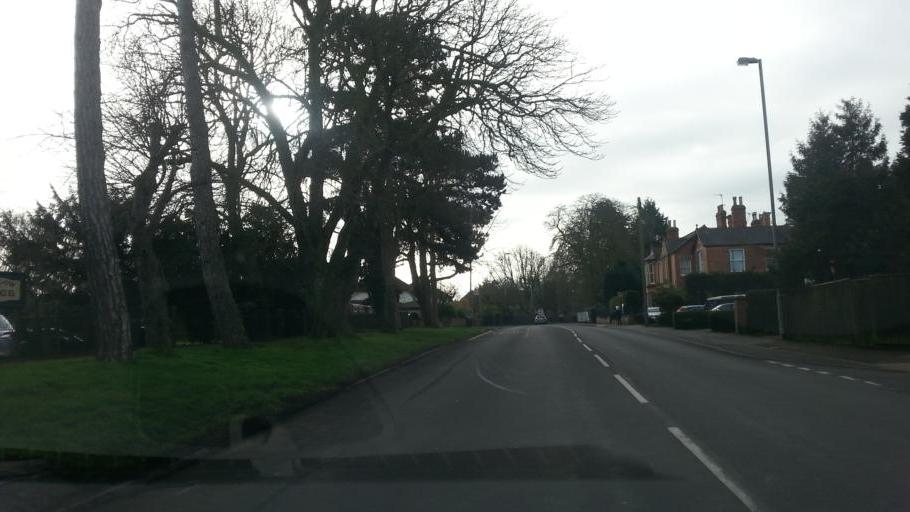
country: GB
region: England
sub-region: Leicestershire
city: Melton Mowbray
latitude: 52.7568
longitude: -0.8806
